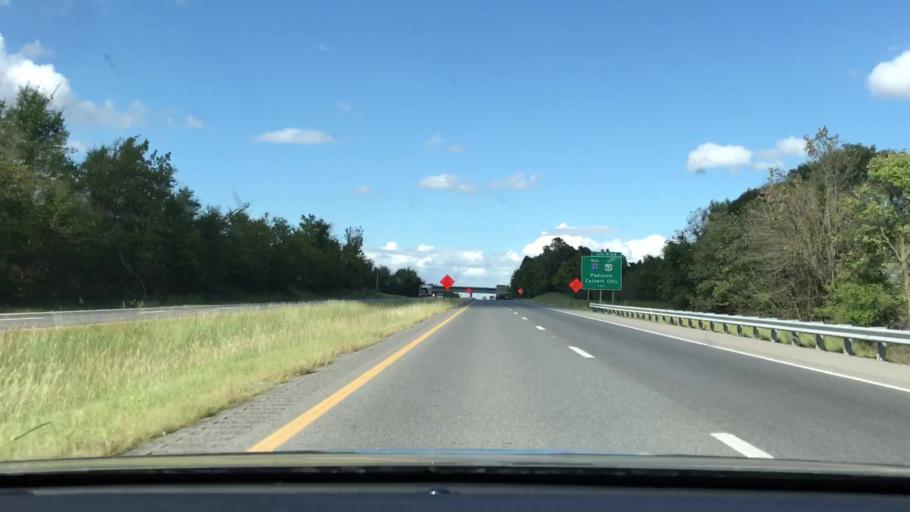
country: US
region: Kentucky
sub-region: Marshall County
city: Calvert City
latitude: 36.9640
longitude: -88.3479
